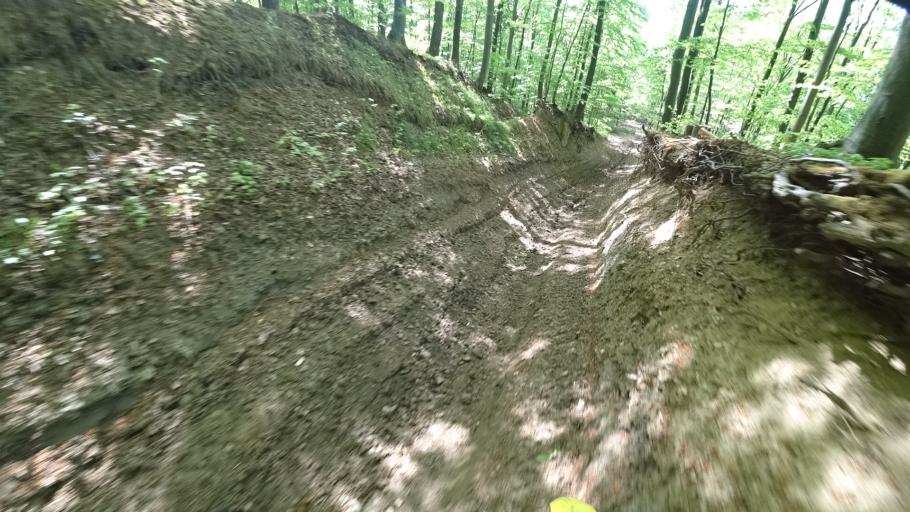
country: HR
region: Zagrebacka
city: Jablanovec
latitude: 45.8893
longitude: 15.8942
